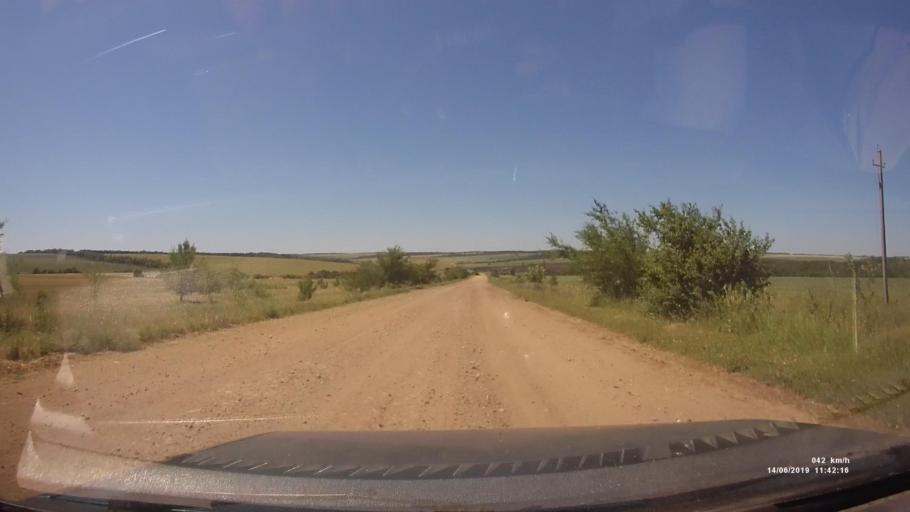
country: RU
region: Rostov
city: Kazanskaya
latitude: 49.8601
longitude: 41.3453
